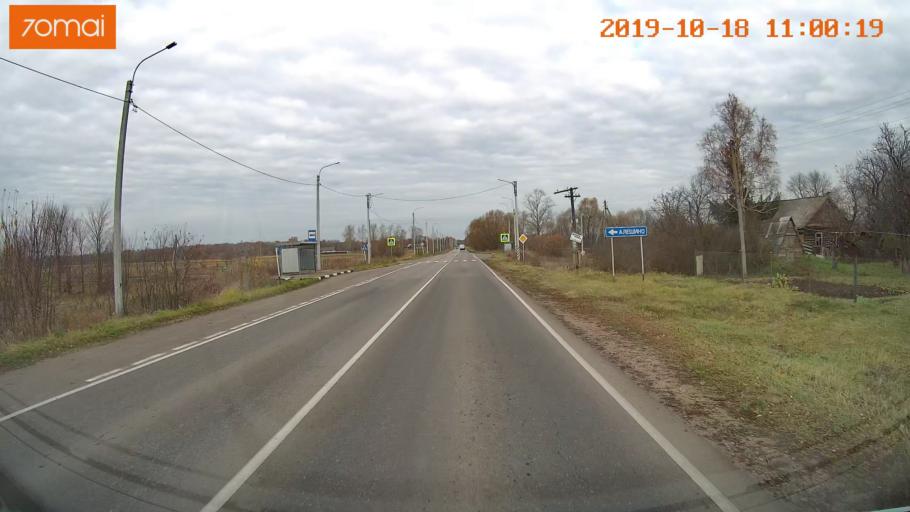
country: RU
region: Tula
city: Yepifan'
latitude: 53.8418
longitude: 38.5527
